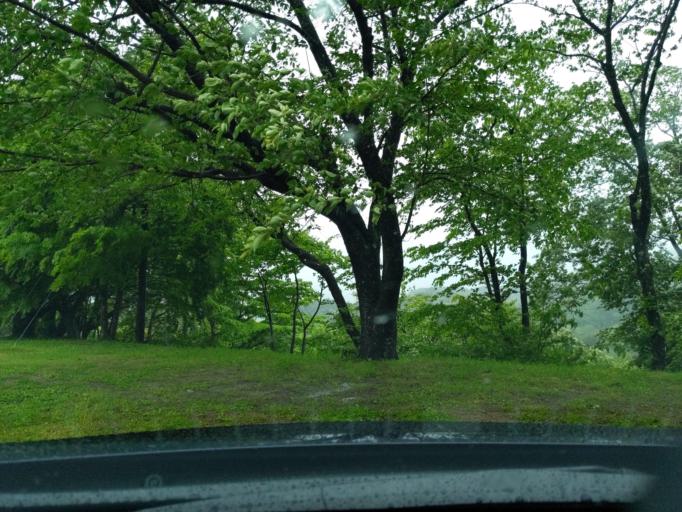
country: JP
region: Fukushima
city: Hobaramachi
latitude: 37.6691
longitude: 140.6499
